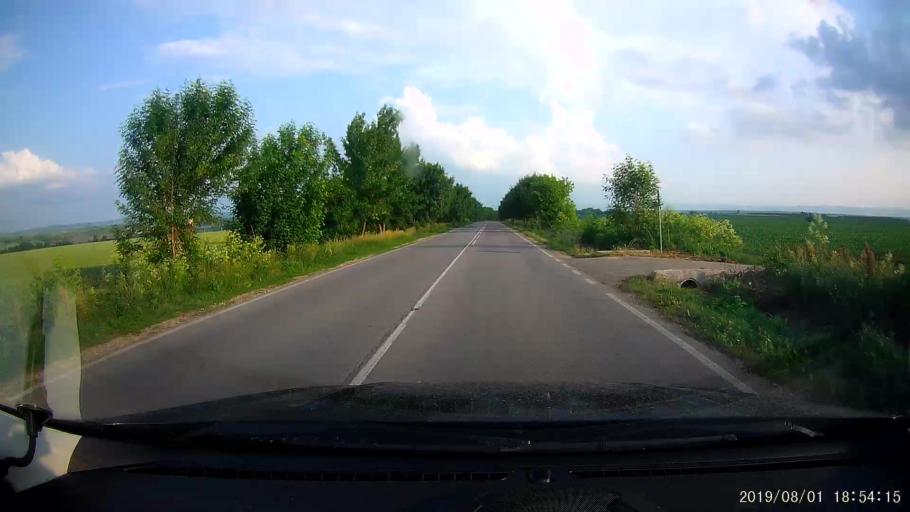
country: BG
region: Shumen
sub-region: Obshtina Shumen
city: Shumen
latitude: 43.2032
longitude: 27.0006
